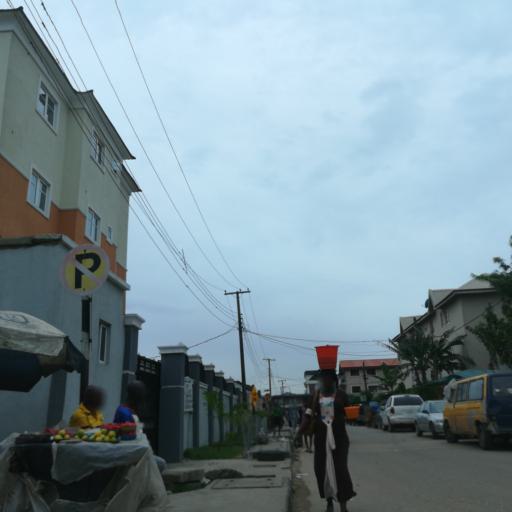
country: NG
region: Lagos
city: Makoko
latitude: 6.5010
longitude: 3.3809
